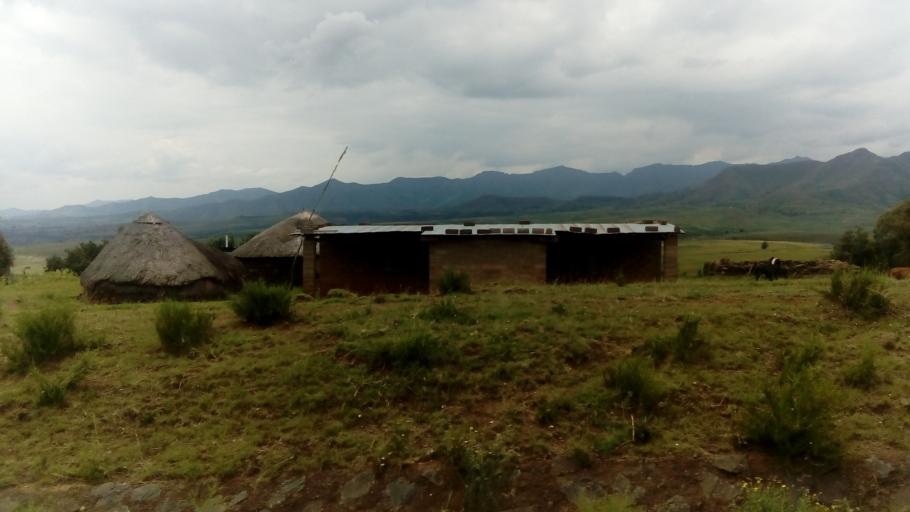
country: LS
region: Leribe
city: Leribe
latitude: -29.0271
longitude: 28.2313
